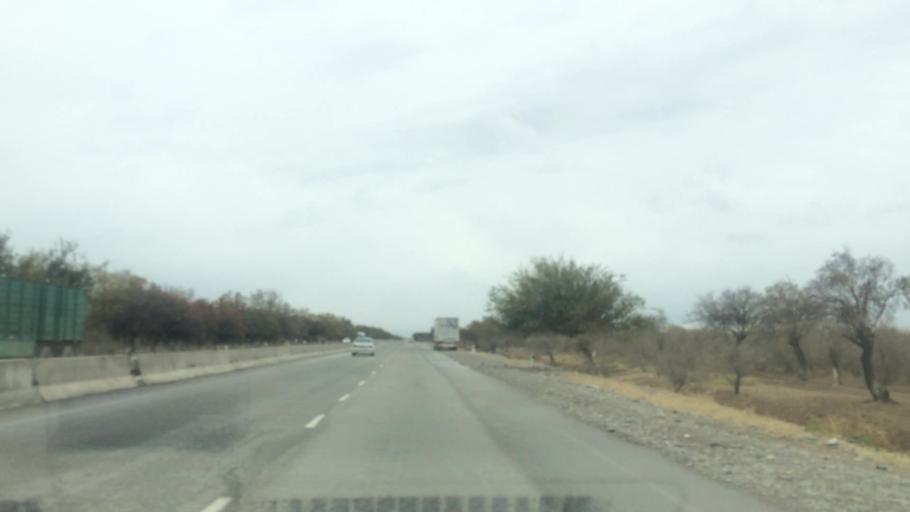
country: UZ
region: Samarqand
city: Bulung'ur
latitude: 39.8179
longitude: 67.3830
